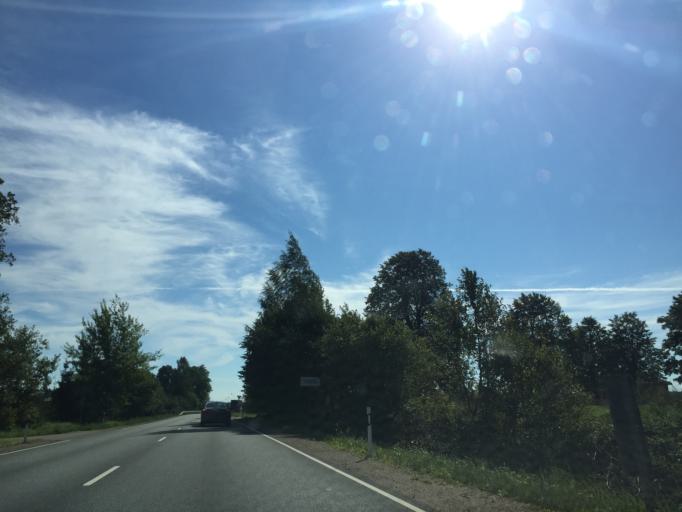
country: LV
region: Ikskile
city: Ikskile
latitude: 56.8662
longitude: 24.5553
